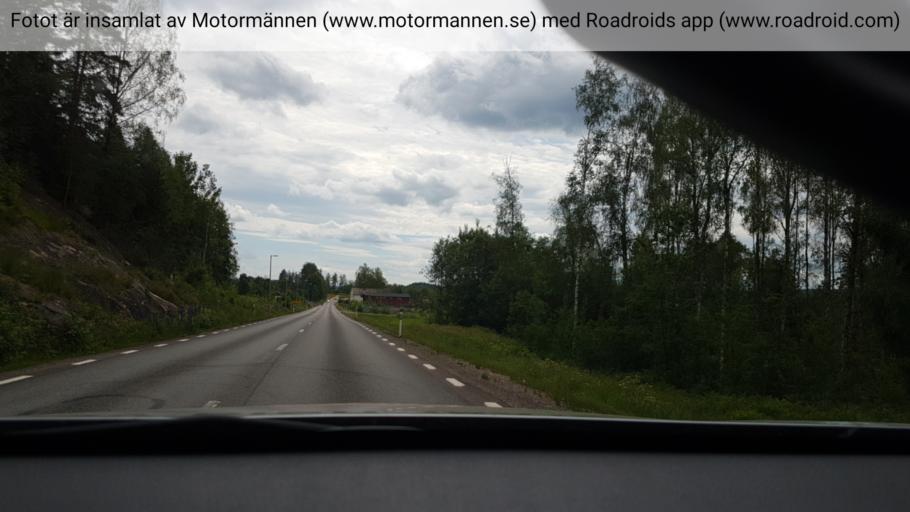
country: SE
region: Vaermland
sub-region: Torsby Kommun
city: Torsby
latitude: 60.2389
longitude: 13.0100
